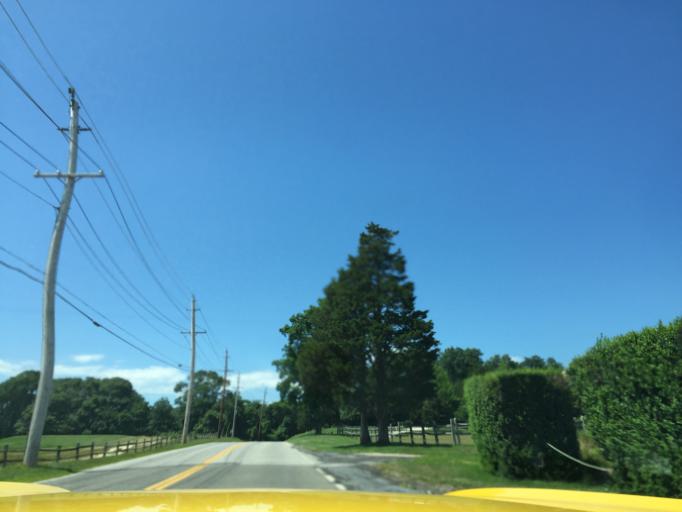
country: US
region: New York
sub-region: Suffolk County
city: Amagansett
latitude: 40.9834
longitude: -72.1338
